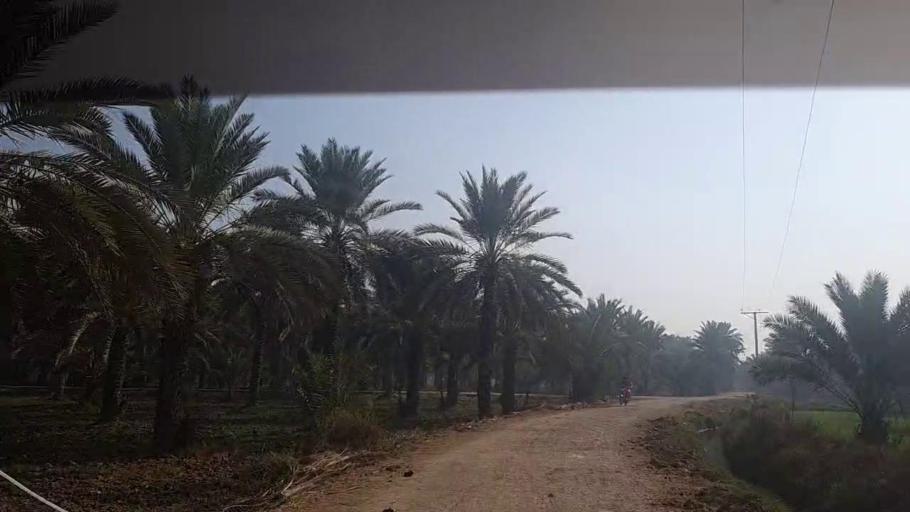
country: PK
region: Sindh
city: Khairpur
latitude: 27.4789
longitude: 68.7195
